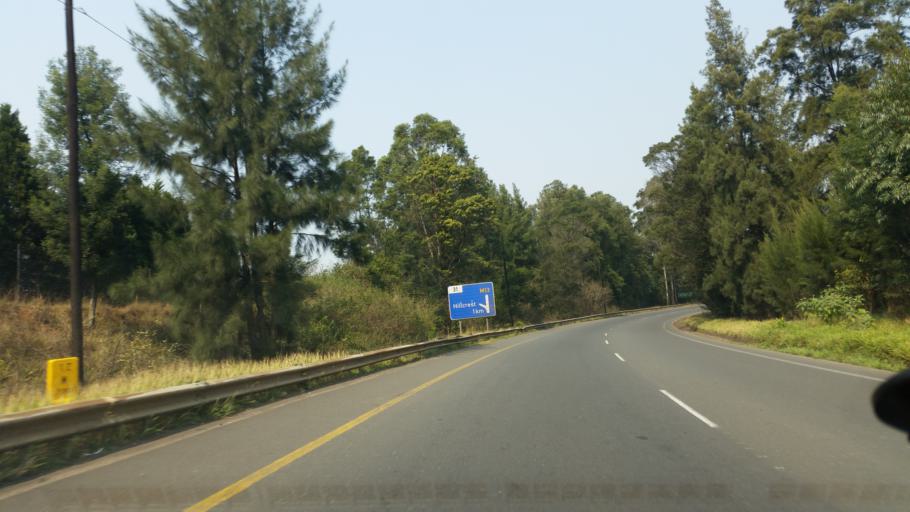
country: ZA
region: KwaZulu-Natal
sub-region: eThekwini Metropolitan Municipality
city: Mpumalanga
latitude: -29.8001
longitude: 30.7748
